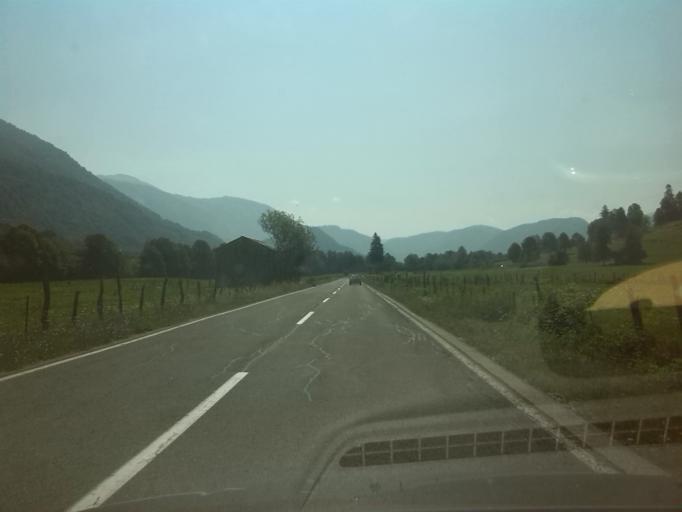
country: SI
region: Tolmin
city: Tolmin
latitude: 46.2026
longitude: 13.6833
